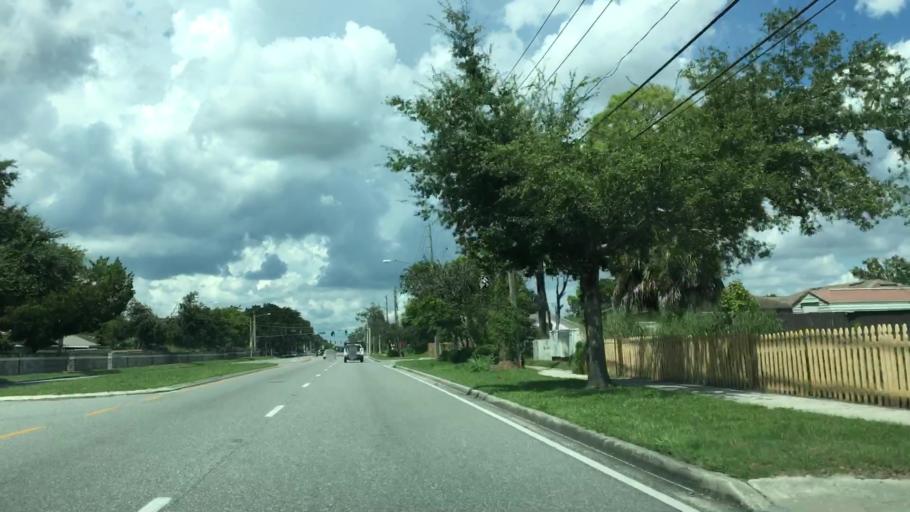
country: US
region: Florida
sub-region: Orange County
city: Conway
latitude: 28.4991
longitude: -81.2913
